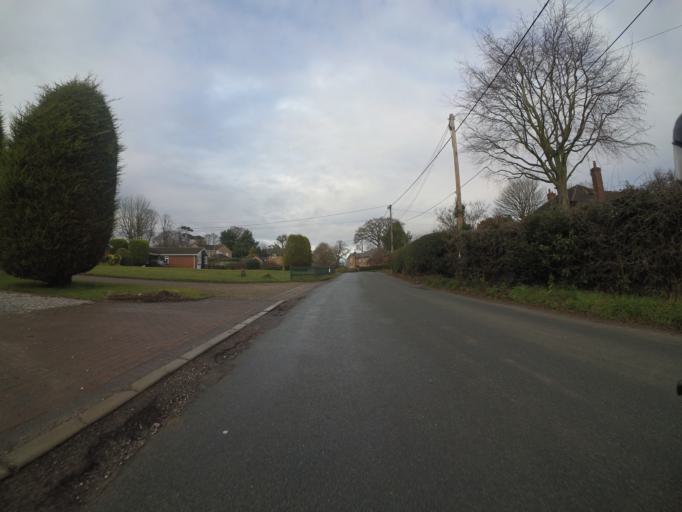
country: GB
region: England
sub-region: Cheshire West and Chester
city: Tiverton
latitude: 53.1199
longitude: -2.6596
